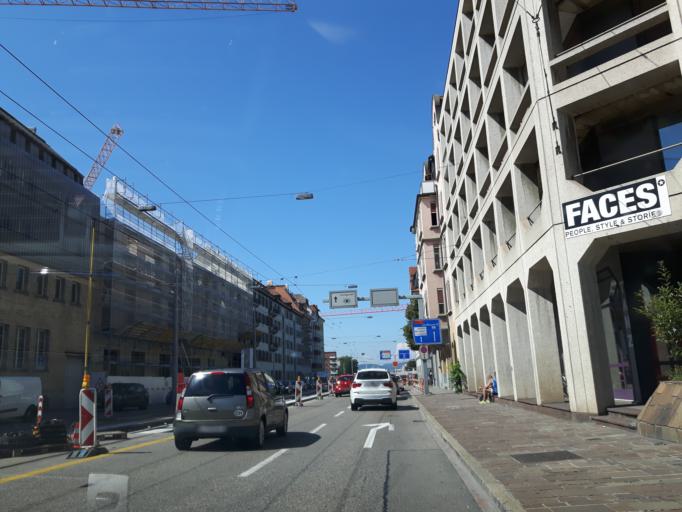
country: CH
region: Zurich
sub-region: Bezirk Zuerich
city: Aussersihl
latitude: 47.3814
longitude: 8.5175
